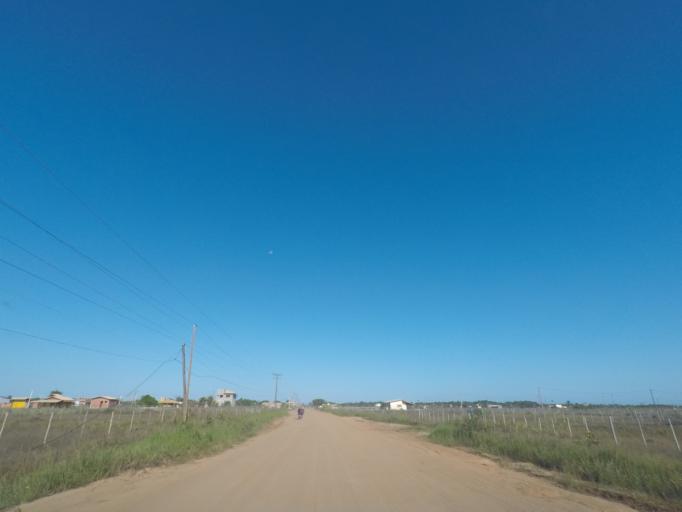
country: BR
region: Bahia
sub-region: Camamu
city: Camamu
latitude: -13.9327
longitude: -38.9448
